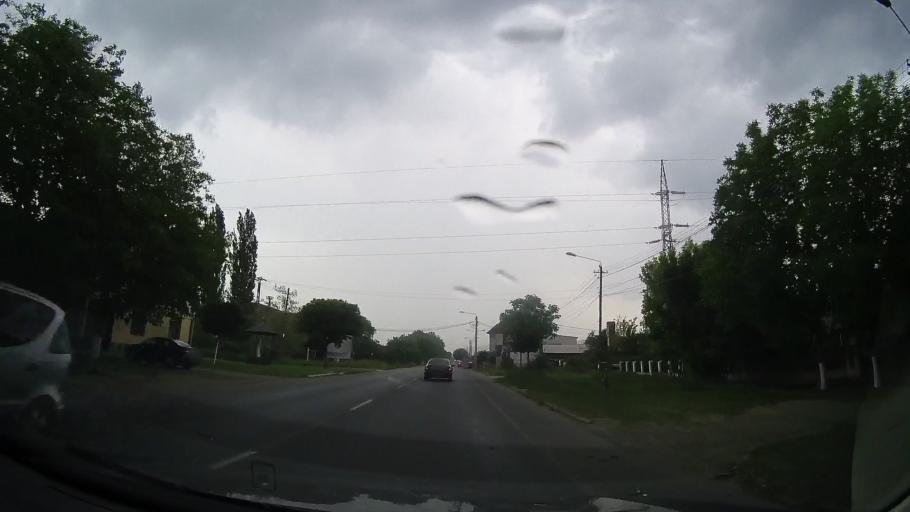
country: RO
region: Caras-Severin
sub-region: Municipiul Caransebes
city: Caransebes
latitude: 45.3947
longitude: 22.2265
